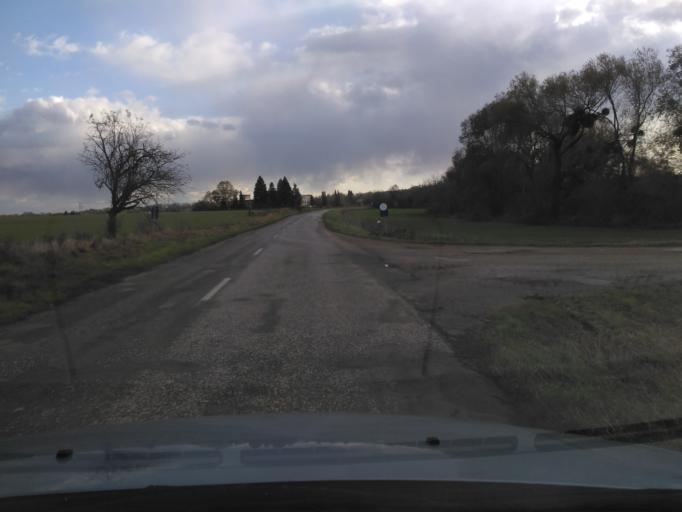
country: HU
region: Borsod-Abauj-Zemplen
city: Satoraljaujhely
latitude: 48.4018
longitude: 21.7091
